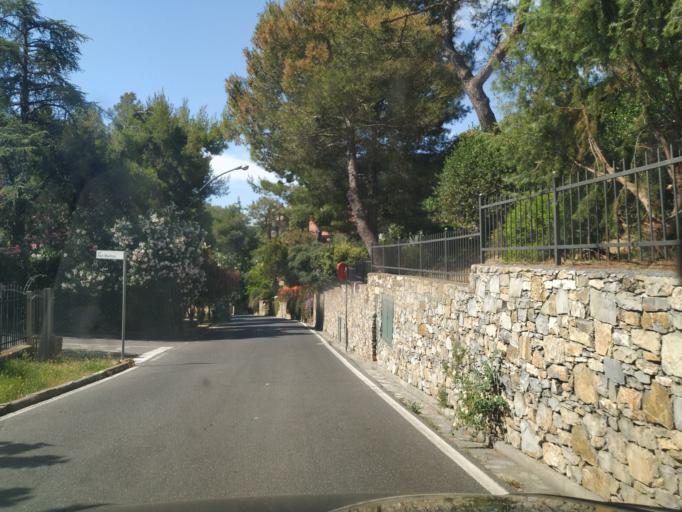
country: IT
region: Liguria
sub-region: Provincia di Savona
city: Marina di Andora
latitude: 43.9546
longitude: 8.1599
